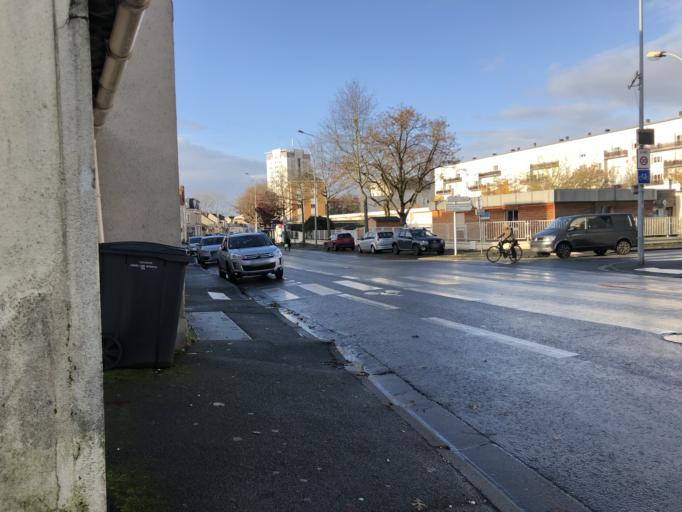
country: FR
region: Pays de la Loire
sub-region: Departement de Maine-et-Loire
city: Angers
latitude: 47.4686
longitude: -0.5324
